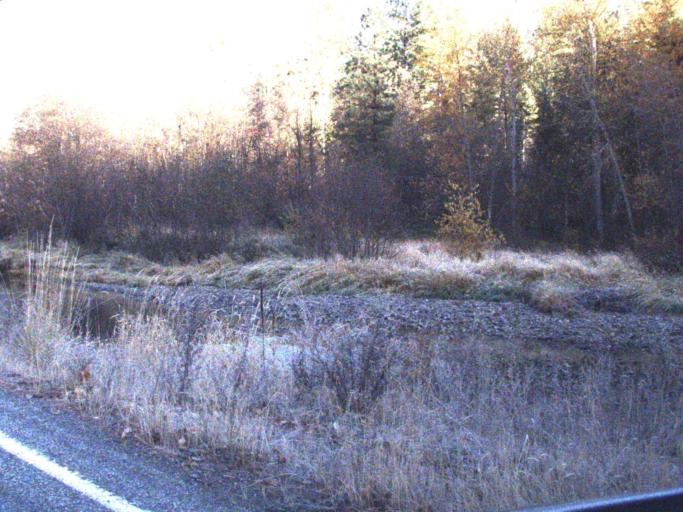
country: US
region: Washington
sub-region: Ferry County
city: Republic
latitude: 48.4320
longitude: -118.7314
